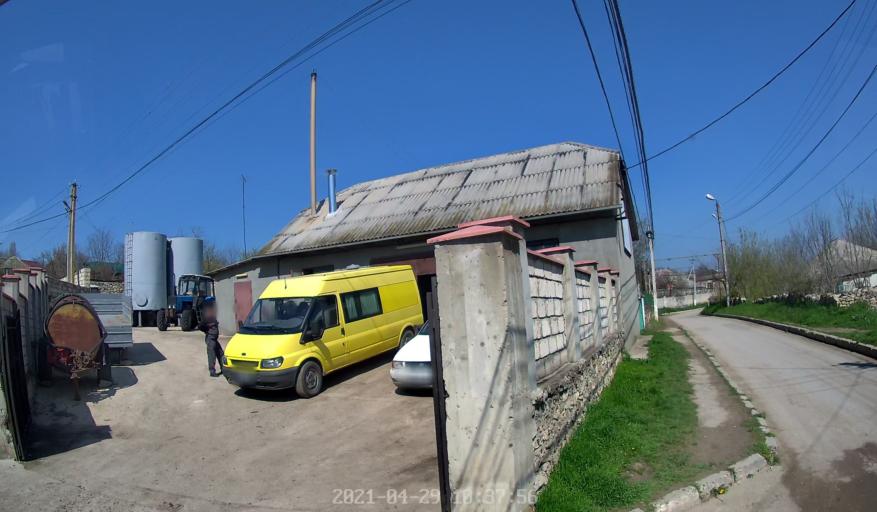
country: MD
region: Chisinau
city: Ciorescu
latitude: 47.1668
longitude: 28.9513
